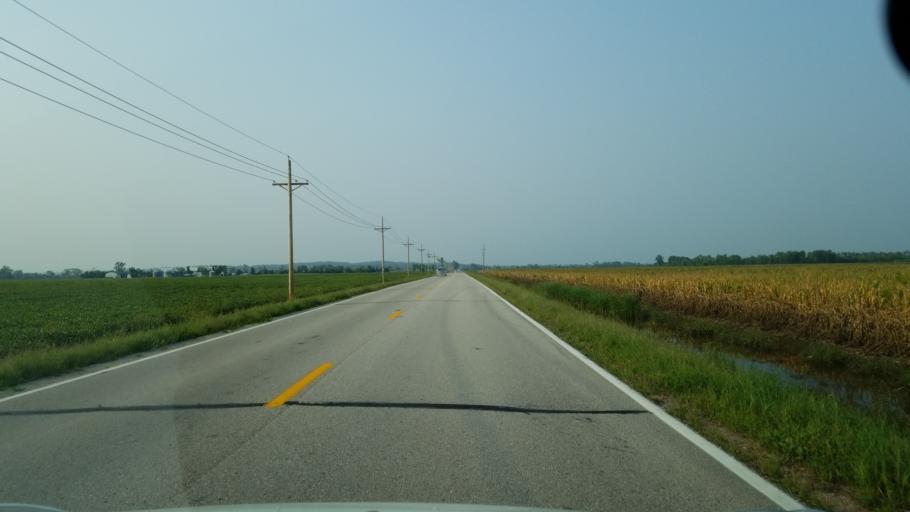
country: US
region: Nebraska
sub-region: Sarpy County
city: Offutt Air Force Base
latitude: 41.0871
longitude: -95.8898
